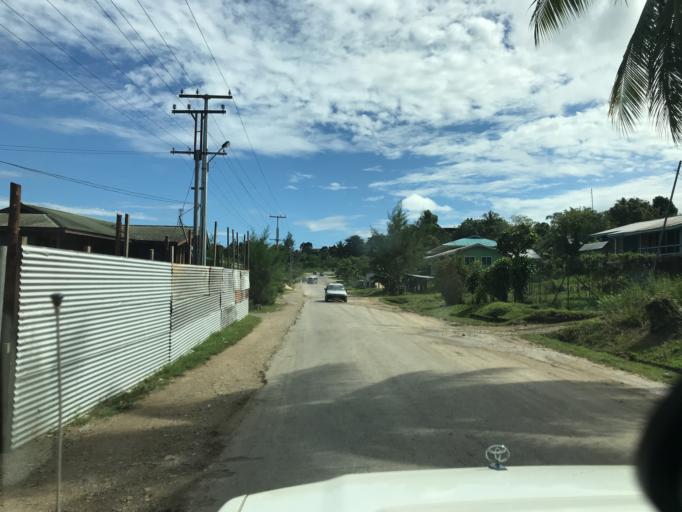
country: SB
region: Malaita
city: Auki
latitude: -8.7667
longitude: 160.6967
